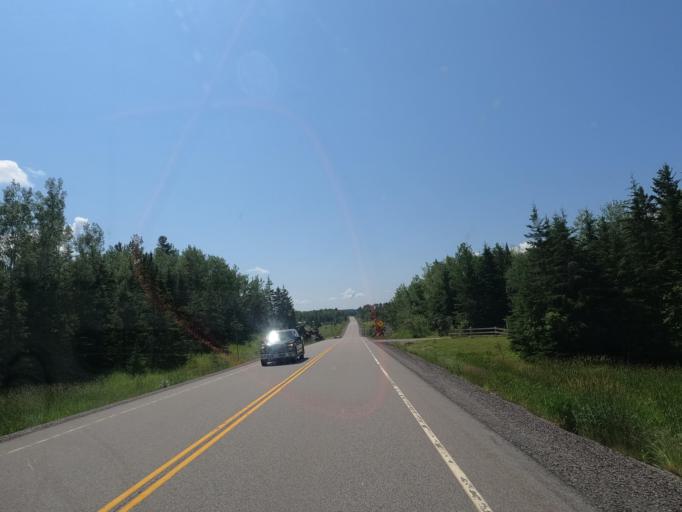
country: CA
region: Ontario
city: Dryden
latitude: 49.8830
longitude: -93.3591
